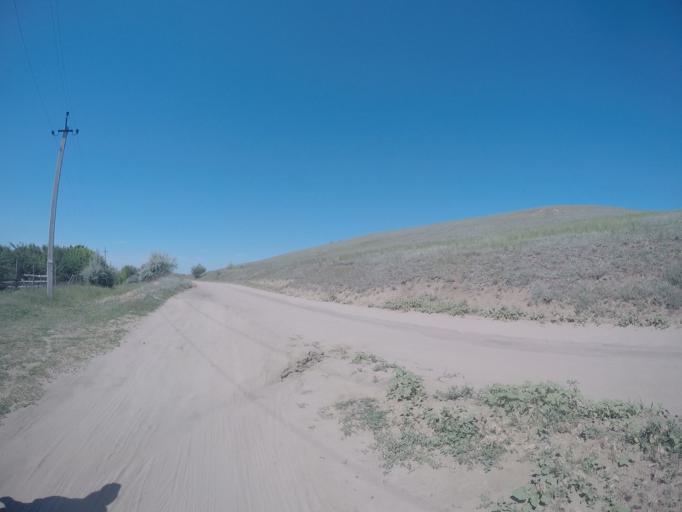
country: RU
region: Saratov
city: Krasnoarmeysk
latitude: 51.1607
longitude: 45.9282
